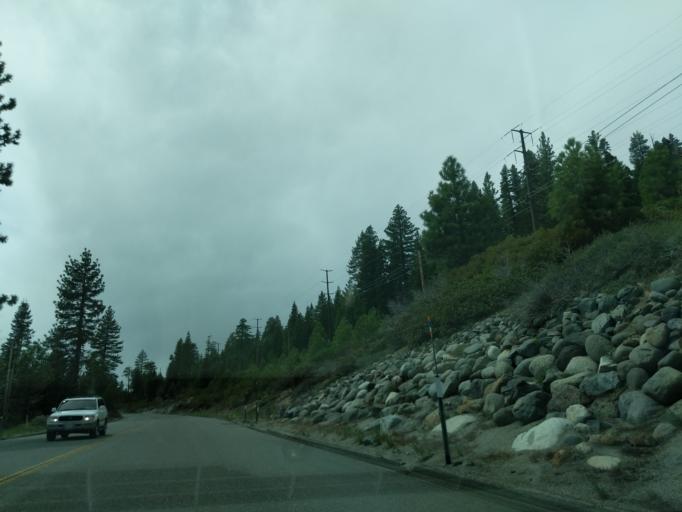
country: US
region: California
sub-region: Placer County
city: Tahoe Vista
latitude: 39.2585
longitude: -120.0609
